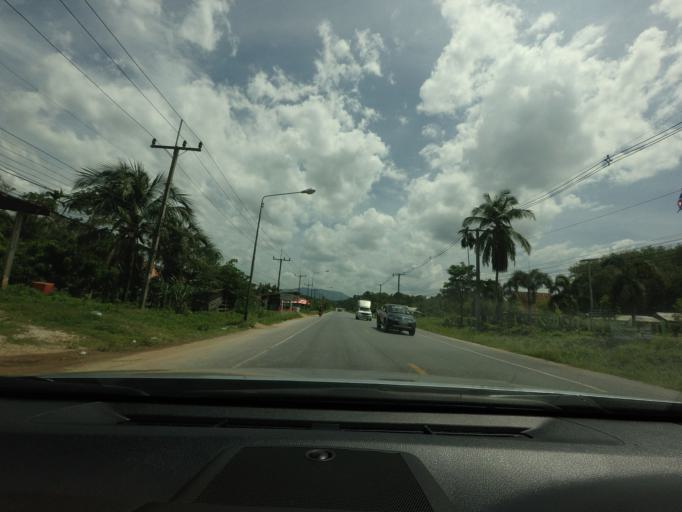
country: TH
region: Yala
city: Raman
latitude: 6.4725
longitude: 101.3983
